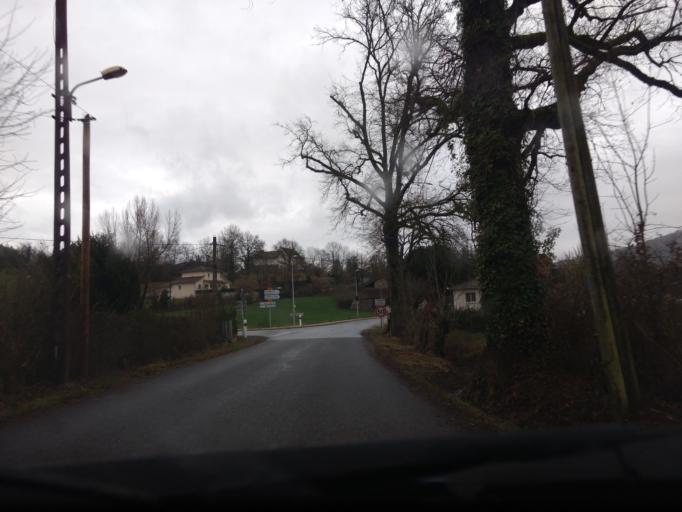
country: FR
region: Midi-Pyrenees
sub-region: Departement de l'Aveyron
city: Livinhac-le-Haut
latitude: 44.6002
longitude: 2.2318
